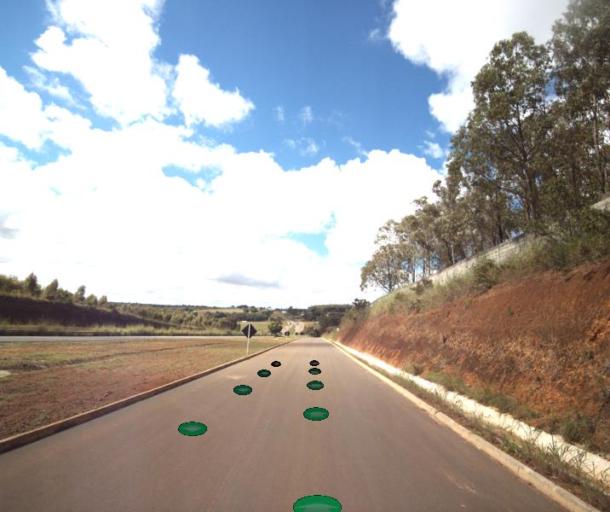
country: BR
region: Goias
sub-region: Anapolis
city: Anapolis
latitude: -16.2395
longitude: -49.0048
